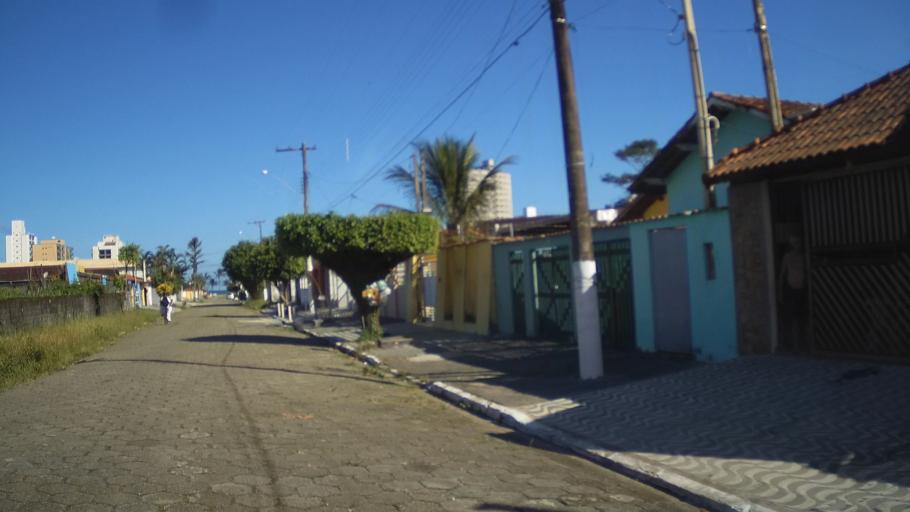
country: BR
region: Sao Paulo
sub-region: Mongagua
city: Mongagua
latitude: -24.0605
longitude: -46.5554
